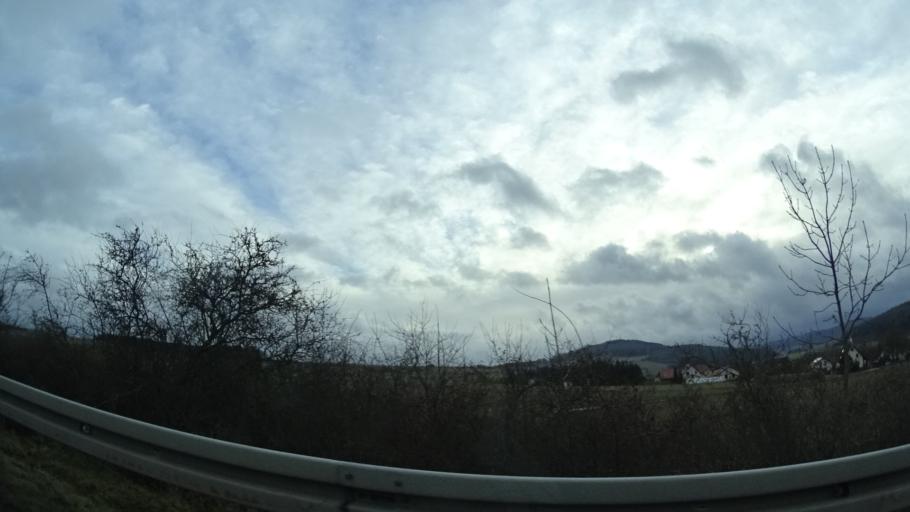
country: DE
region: Thuringia
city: Kaltensundheim
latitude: 50.6080
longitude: 10.1658
